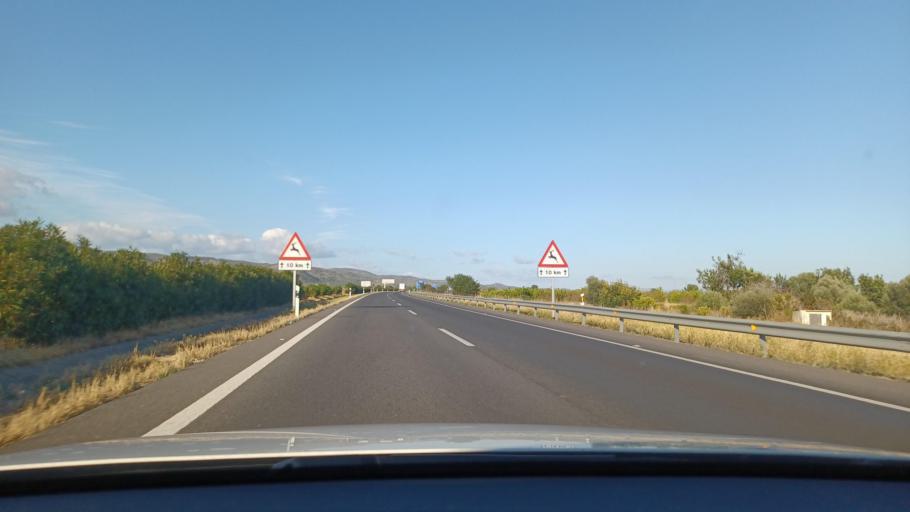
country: ES
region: Valencia
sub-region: Provincia de Castello
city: Orpesa/Oropesa del Mar
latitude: 40.1130
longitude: 0.1311
